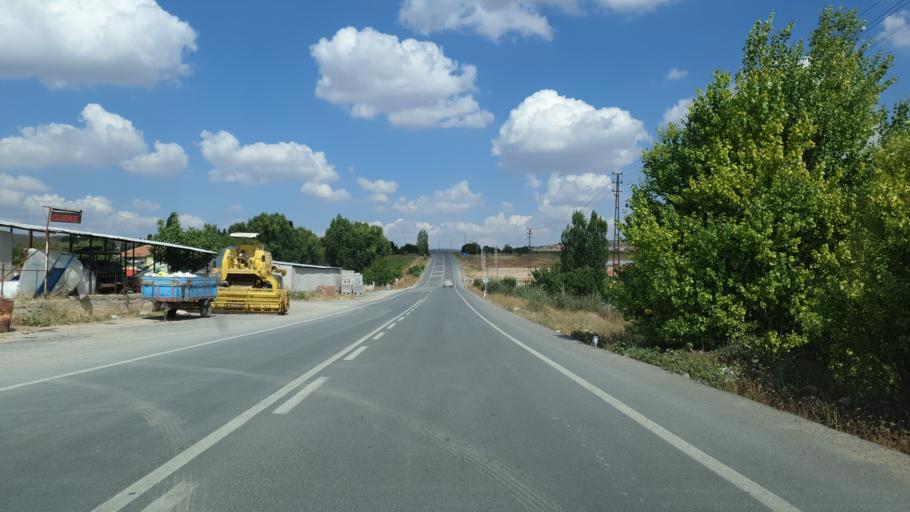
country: TR
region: Kayseri
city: Felahiye
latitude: 39.0948
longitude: 35.5755
